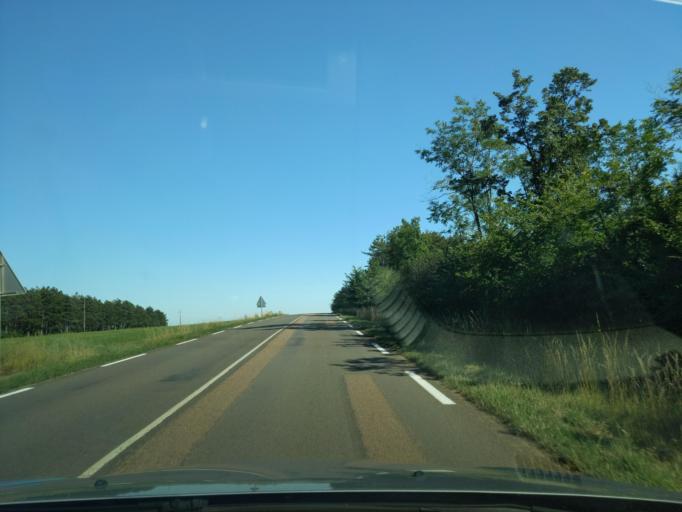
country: FR
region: Bourgogne
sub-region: Departement de la Cote-d'Or
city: Is-sur-Tille
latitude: 47.5041
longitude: 5.0800
